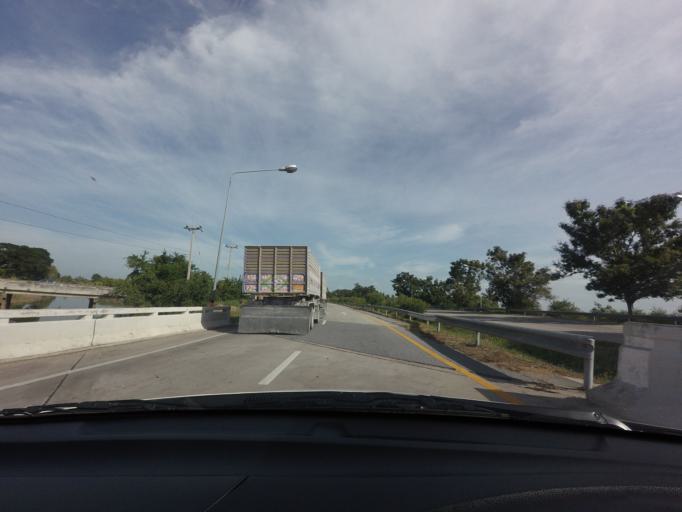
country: TH
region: Suphan Buri
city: Suphan Buri
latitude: 14.4715
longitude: 100.0396
